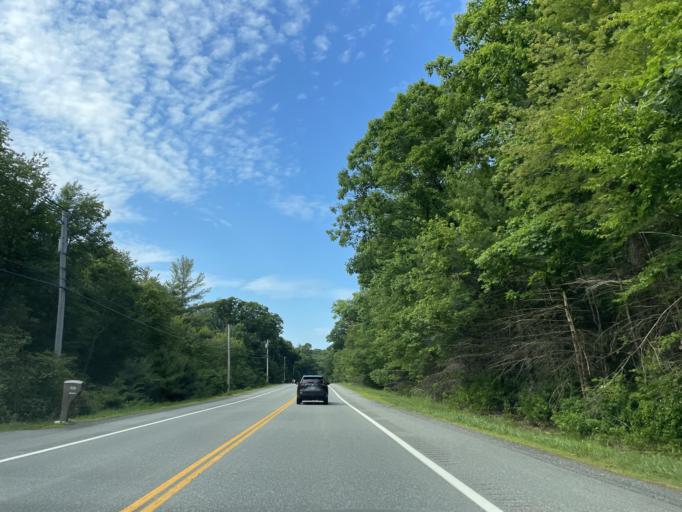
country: US
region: Rhode Island
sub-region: Kent County
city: Coventry
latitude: 41.6717
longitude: -71.6950
